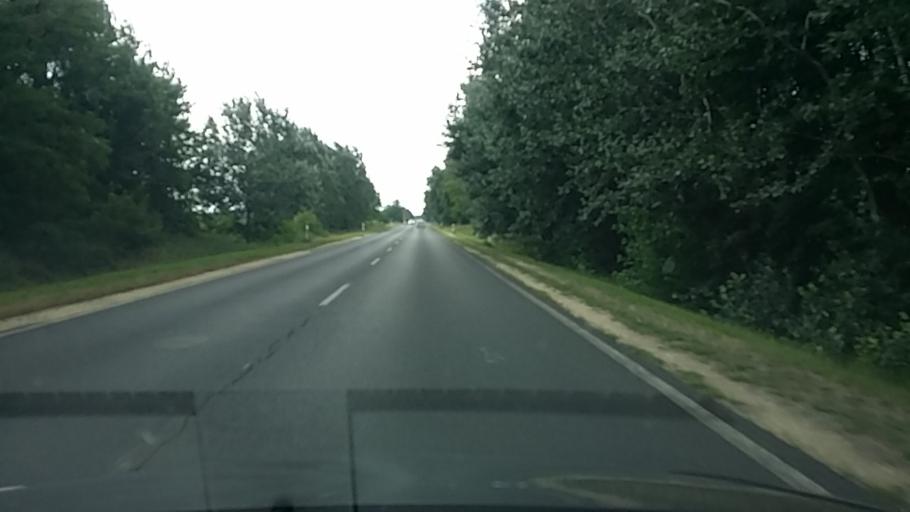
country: HU
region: Pest
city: Taborfalva
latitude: 47.1089
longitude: 19.4586
